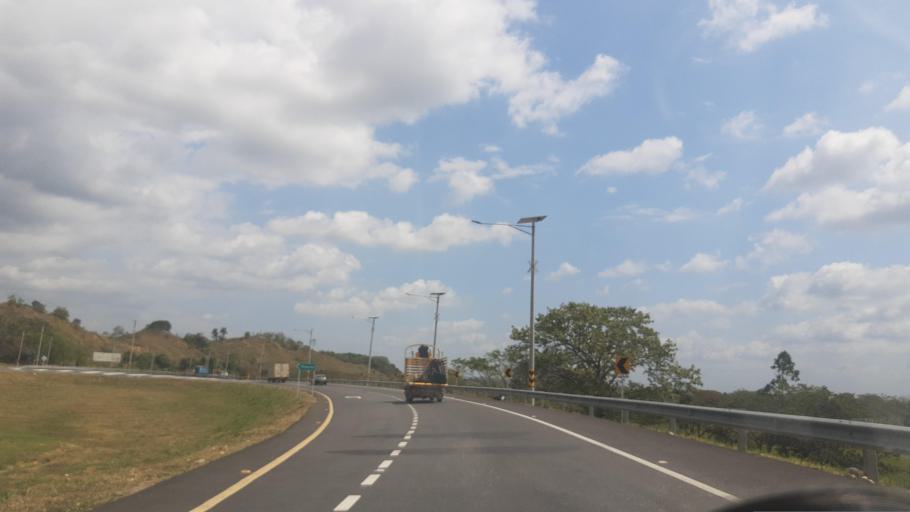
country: CO
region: Casanare
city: Tauramena
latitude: 5.0162
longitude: -72.6730
